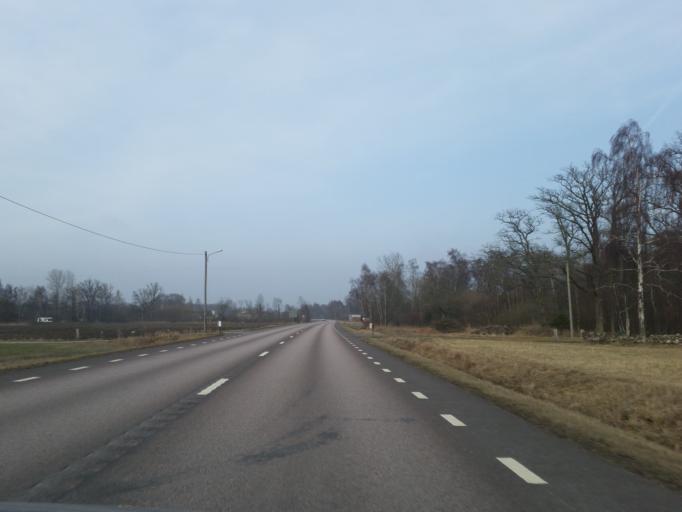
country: SE
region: Kalmar
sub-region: Borgholms Kommun
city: Borgholm
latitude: 57.1068
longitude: 16.9431
